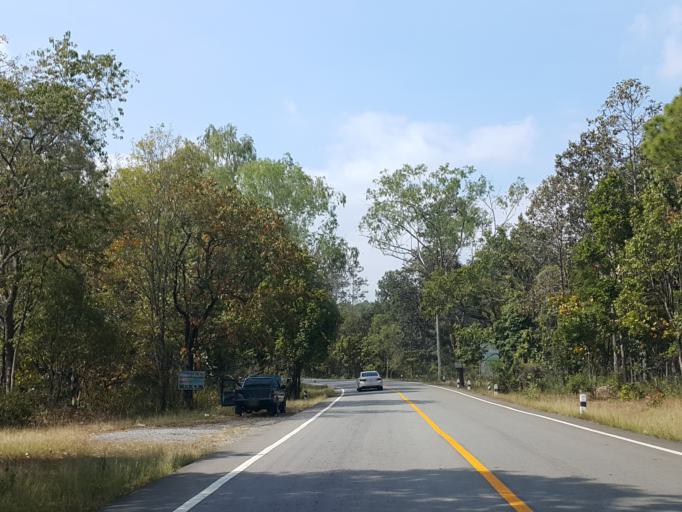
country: TH
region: Chiang Mai
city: Hot
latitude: 18.1586
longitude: 98.3970
